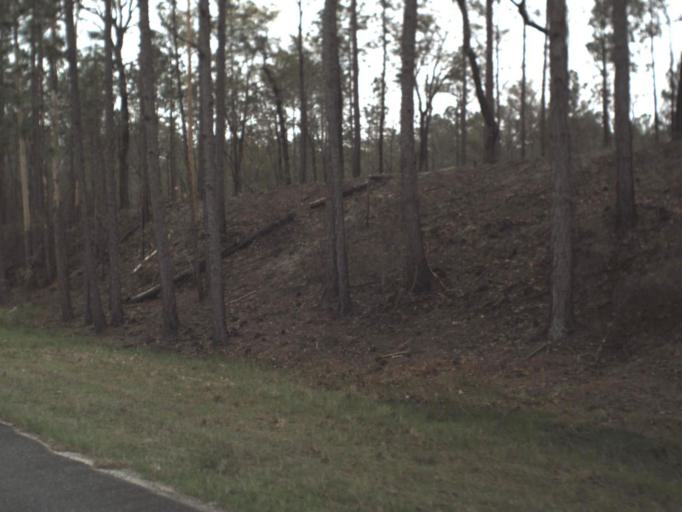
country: US
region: Florida
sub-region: Gadsden County
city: Midway
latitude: 30.3887
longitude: -84.5863
